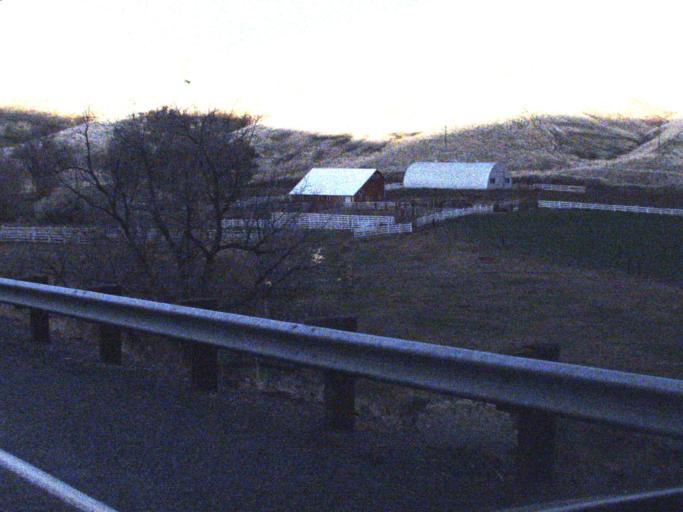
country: US
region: Washington
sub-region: Garfield County
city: Pomeroy
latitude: 46.6000
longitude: -117.7847
